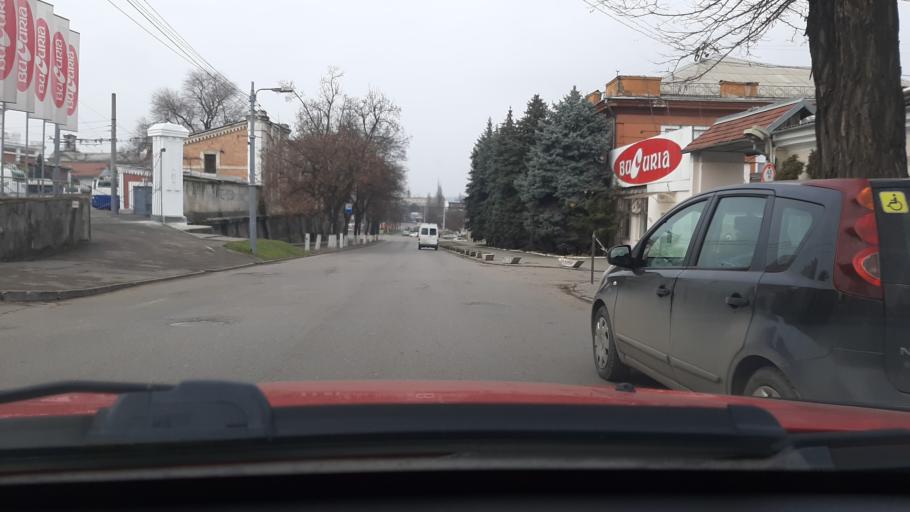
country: MD
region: Chisinau
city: Chisinau
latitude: 47.0350
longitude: 28.8234
